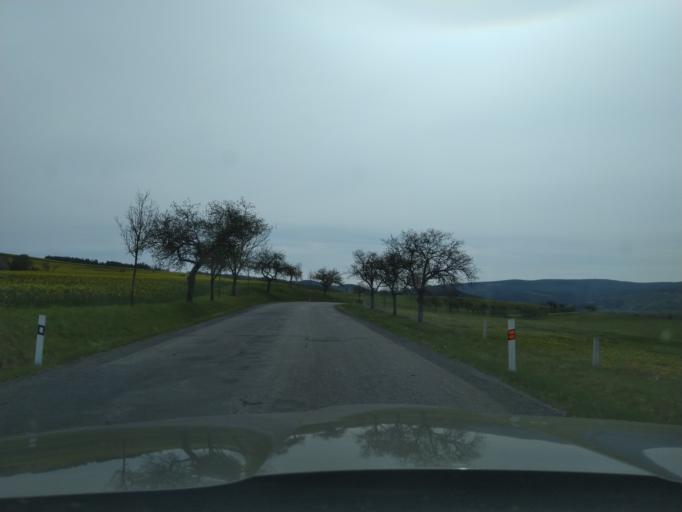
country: CZ
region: Plzensky
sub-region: Okres Klatovy
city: Kasperske Hory
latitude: 49.2019
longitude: 13.6132
